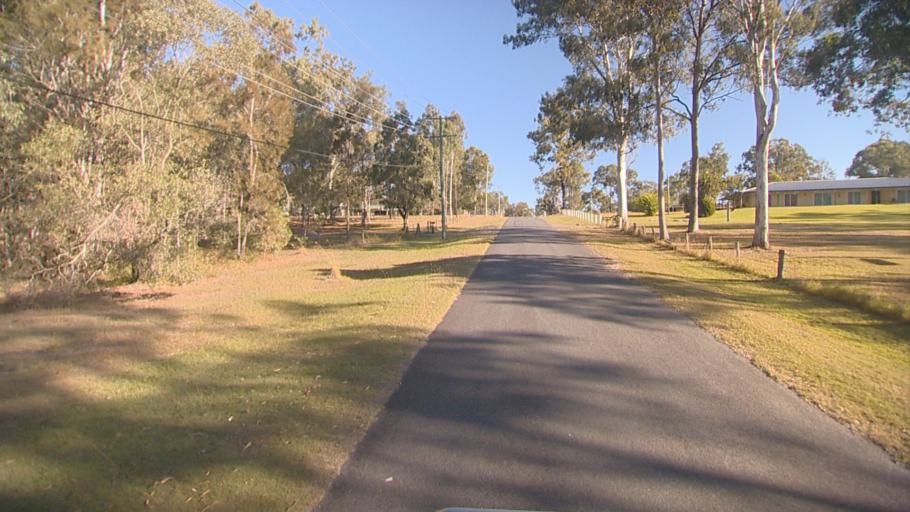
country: AU
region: Queensland
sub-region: Logan
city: Logan Reserve
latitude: -27.7434
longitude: 153.1085
